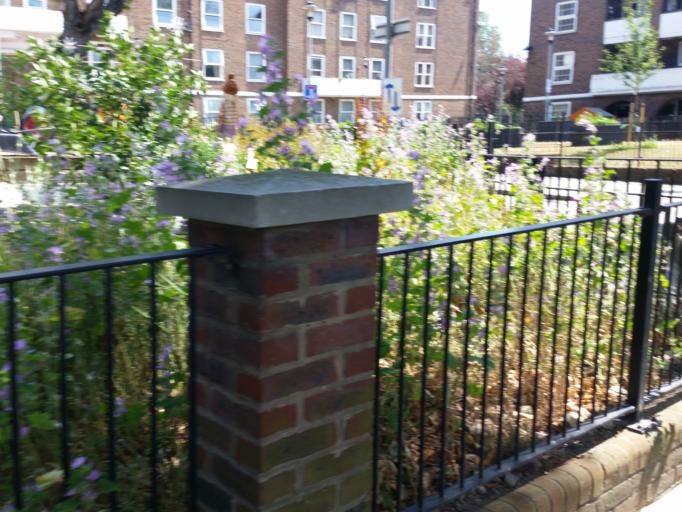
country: GB
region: England
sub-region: Greater London
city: Hackney
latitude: 51.5690
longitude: -0.0728
